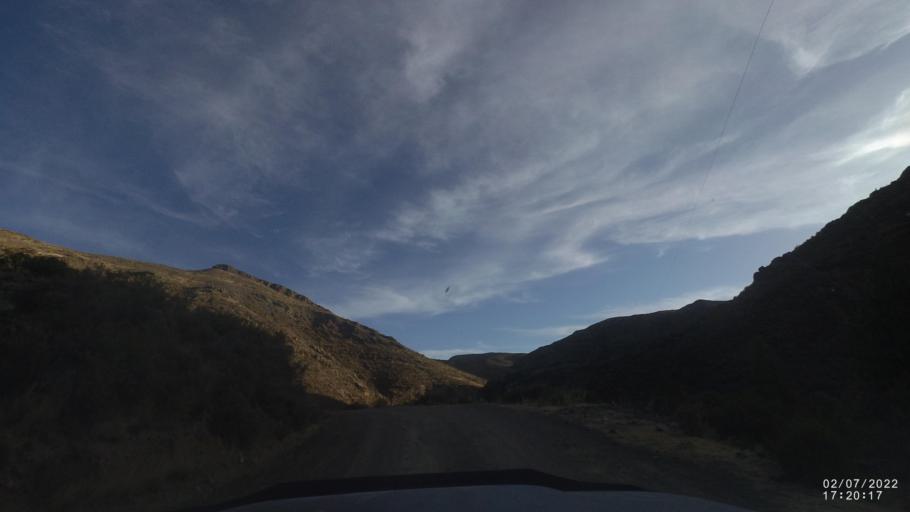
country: BO
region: Cochabamba
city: Irpa Irpa
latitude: -17.8767
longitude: -66.5946
